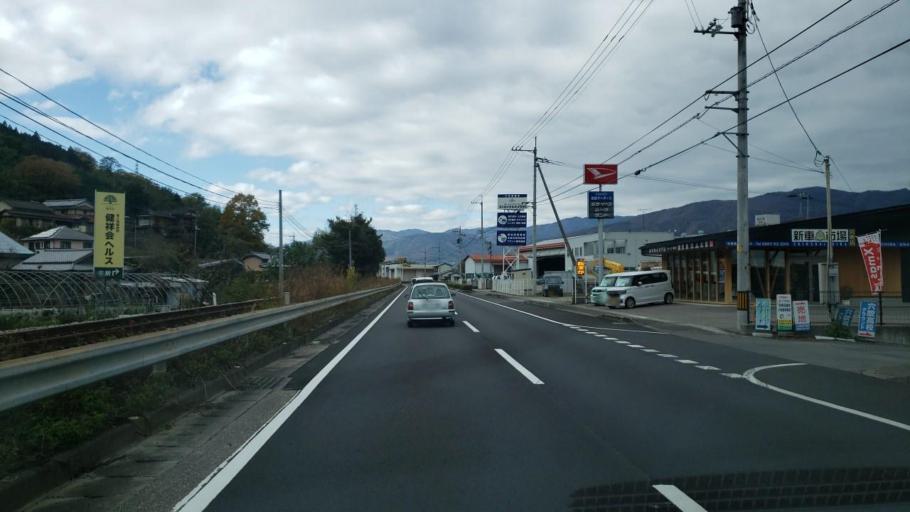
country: JP
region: Tokushima
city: Wakimachi
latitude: 34.0543
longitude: 134.1416
